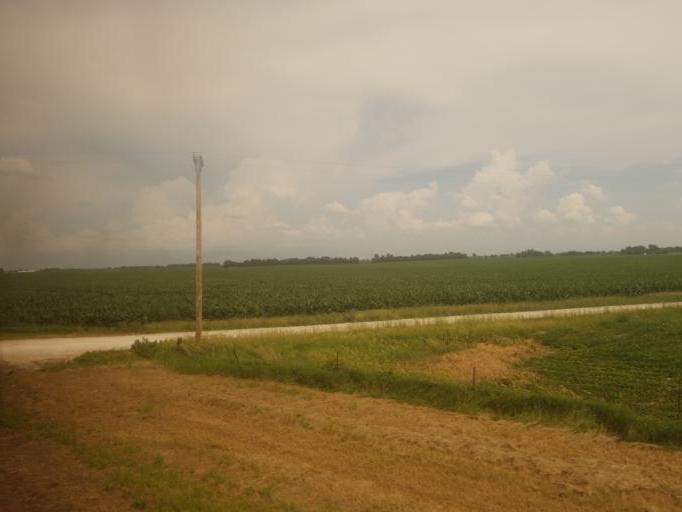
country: US
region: Illinois
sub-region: Knox County
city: Galesburg
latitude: 40.9119
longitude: -90.4230
